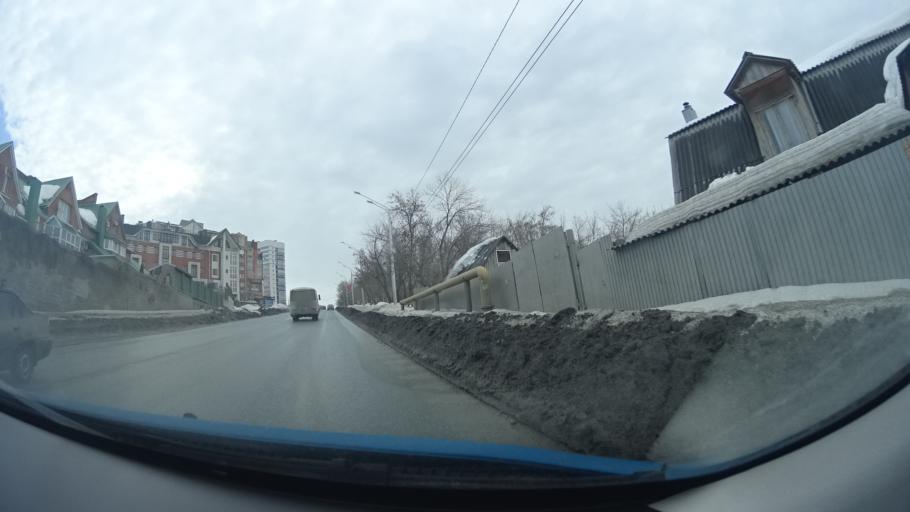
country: RU
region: Bashkortostan
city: Ufa
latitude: 54.7042
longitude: 55.9753
